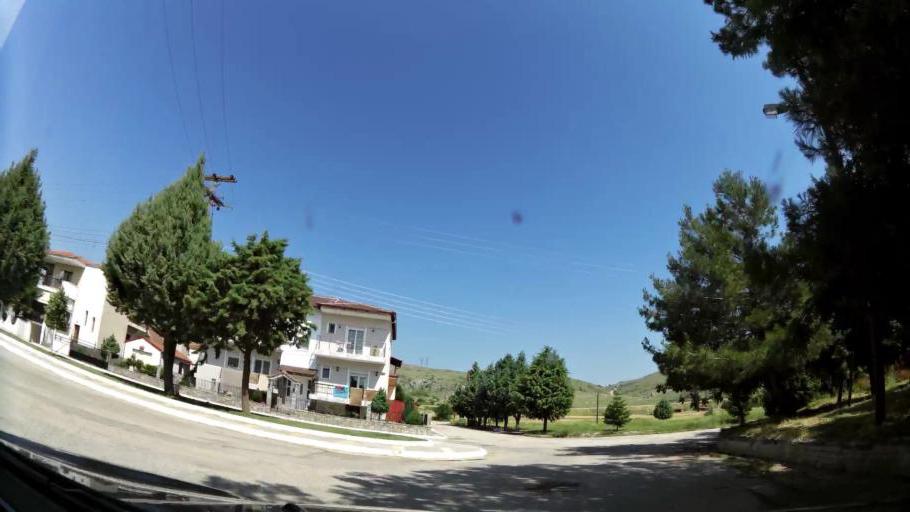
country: GR
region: West Macedonia
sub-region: Nomos Kozanis
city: Koila
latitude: 40.3384
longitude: 21.7878
